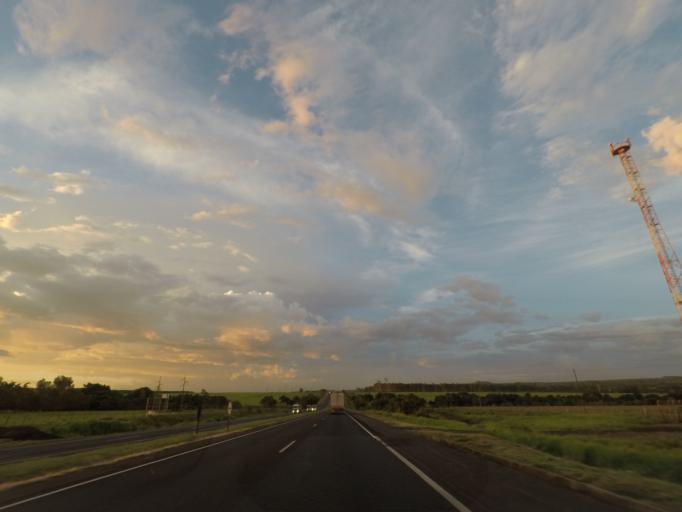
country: BR
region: Minas Gerais
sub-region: Uberaba
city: Uberaba
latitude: -19.6480
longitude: -48.0069
